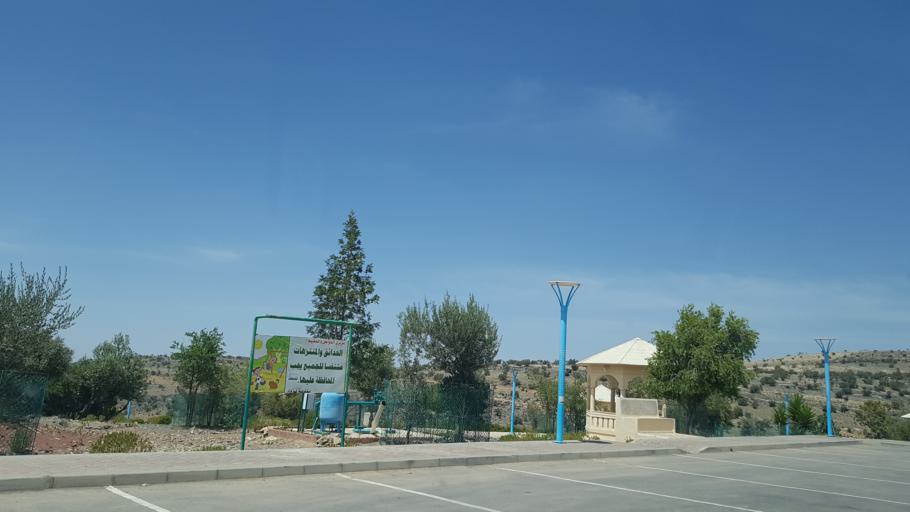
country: OM
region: Al Batinah
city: Bayt al `Awabi
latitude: 23.1327
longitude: 57.5963
